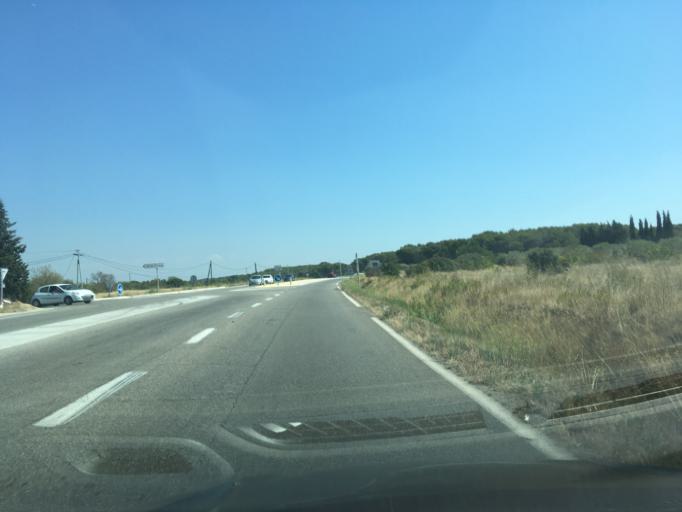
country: FR
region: Provence-Alpes-Cote d'Azur
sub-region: Departement des Bouches-du-Rhone
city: Lancon-Provence
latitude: 43.5846
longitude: 5.1390
